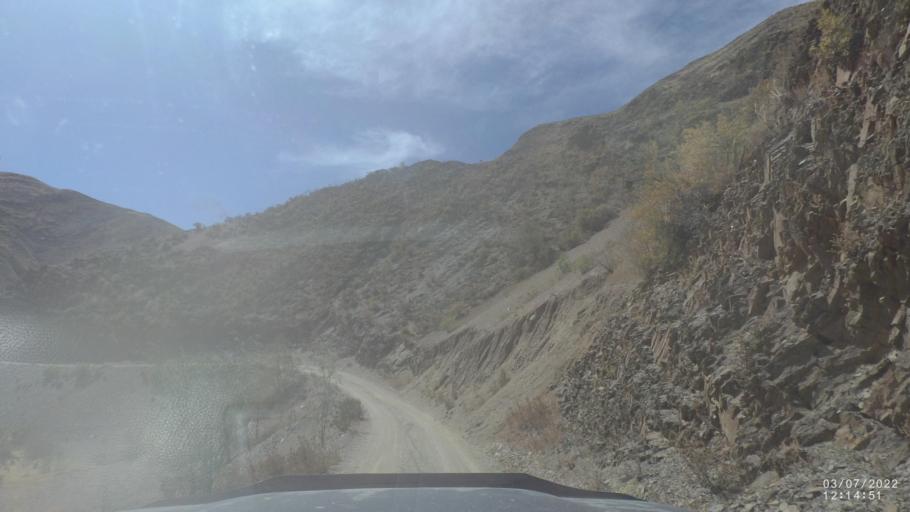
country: BO
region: Cochabamba
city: Irpa Irpa
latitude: -17.8311
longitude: -66.6078
